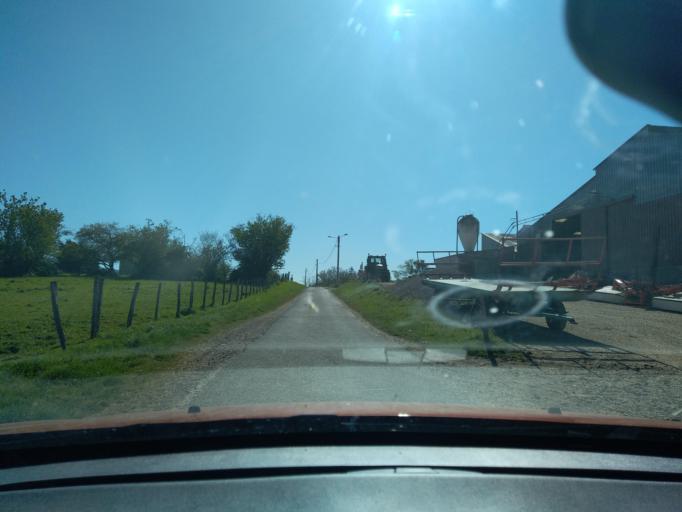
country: FR
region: Franche-Comte
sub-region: Departement du Jura
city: Montmorot
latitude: 46.6100
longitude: 5.4794
